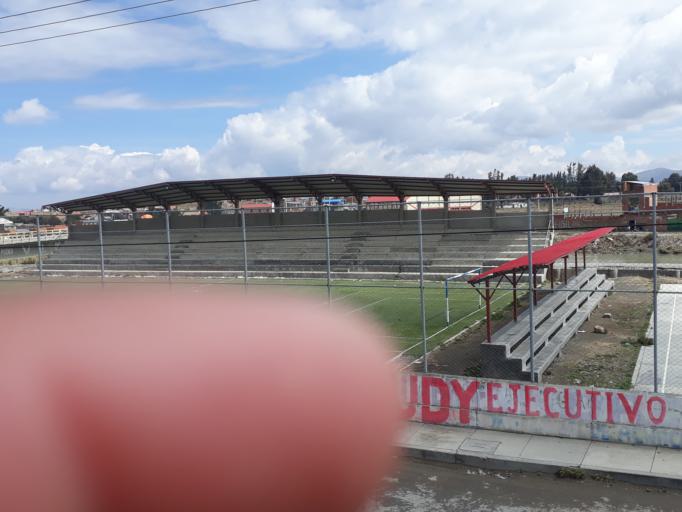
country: BO
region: La Paz
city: Achacachi
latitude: -16.0391
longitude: -68.6857
